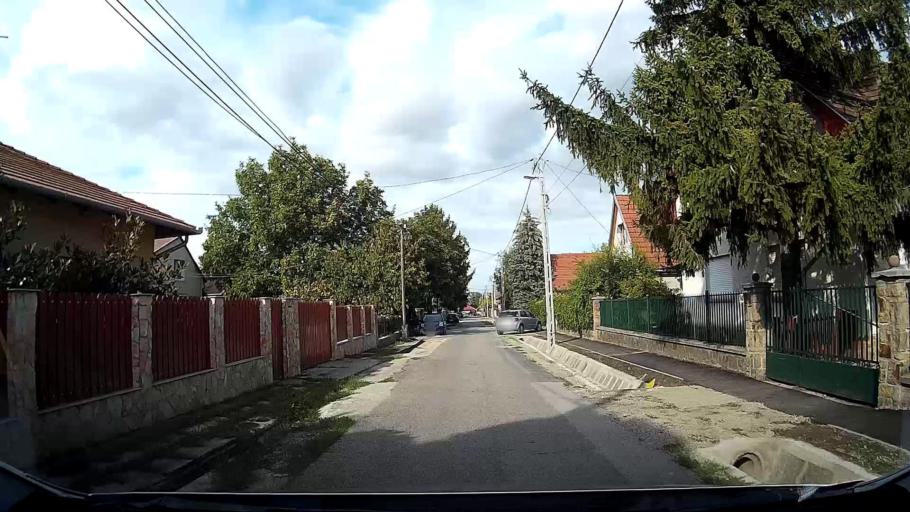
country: HU
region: Pest
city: Pomaz
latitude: 47.6399
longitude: 19.0290
